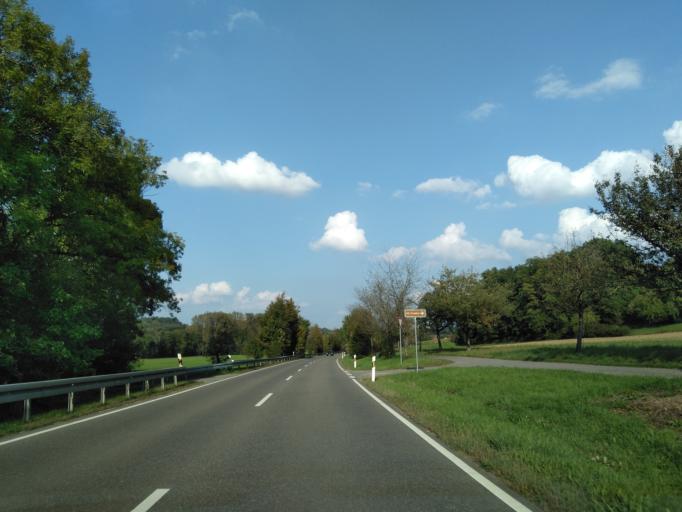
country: DE
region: Baden-Wuerttemberg
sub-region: Regierungsbezirk Stuttgart
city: Oberriexingen
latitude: 48.9328
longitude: 9.0419
